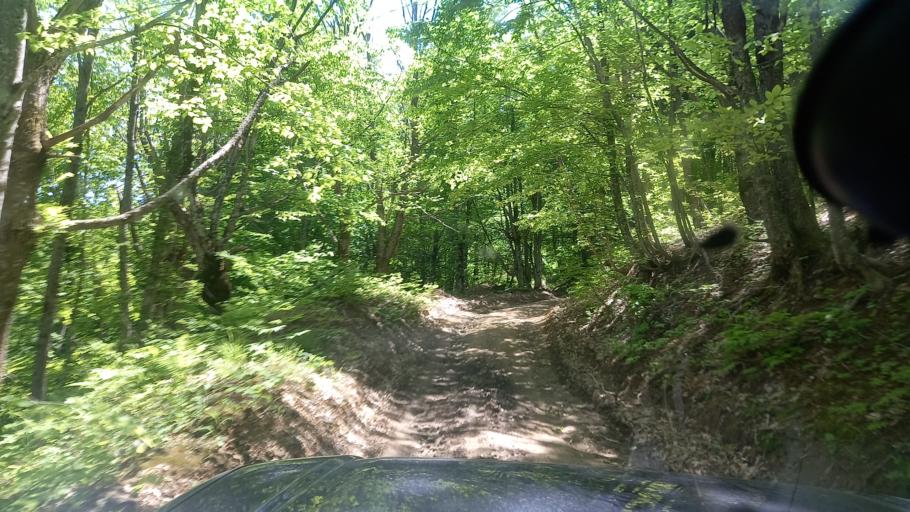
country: RU
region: Krasnodarskiy
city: Tuapse
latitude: 44.2604
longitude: 39.2836
